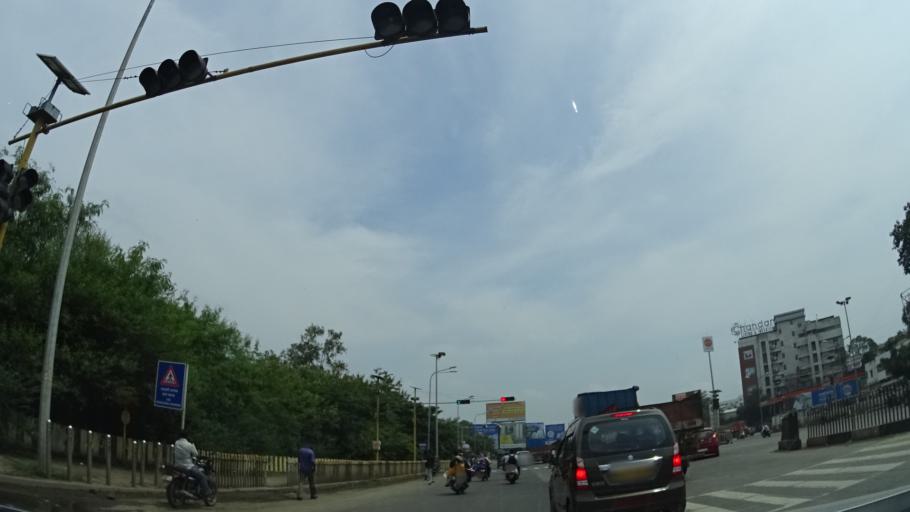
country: IN
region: Maharashtra
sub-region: Pune Division
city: Lohogaon
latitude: 18.5647
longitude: 73.9433
